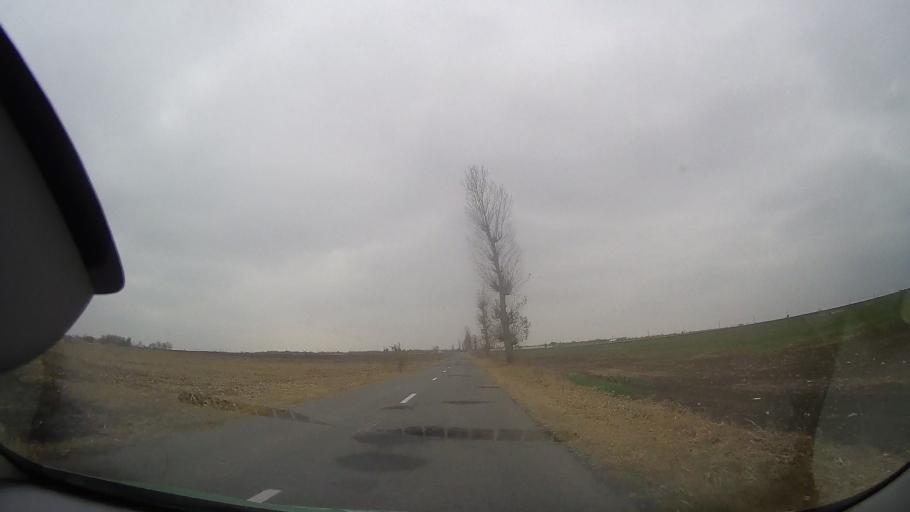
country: RO
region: Ialomita
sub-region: Comuna Valea Macrisului
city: Valea Macrisului
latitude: 44.7349
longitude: 26.8528
